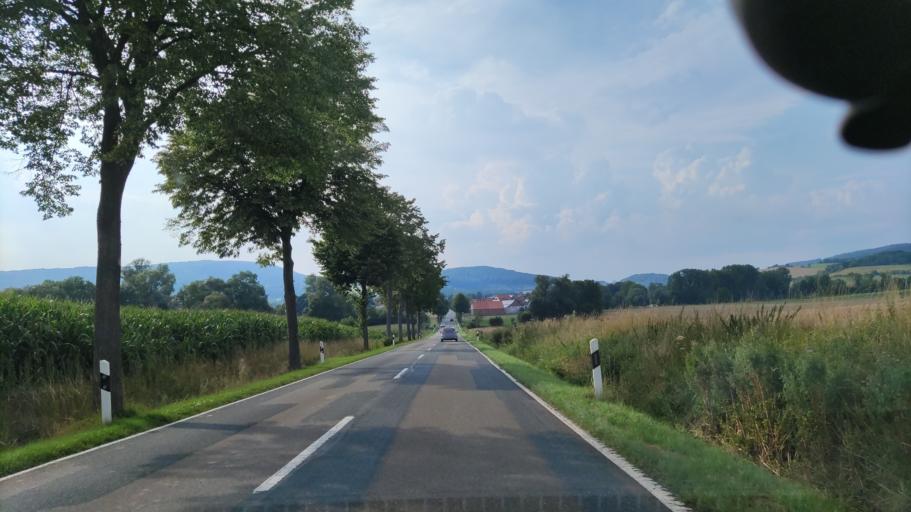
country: DE
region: Lower Saxony
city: Wangelnstedt
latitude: 51.8402
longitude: 9.7333
